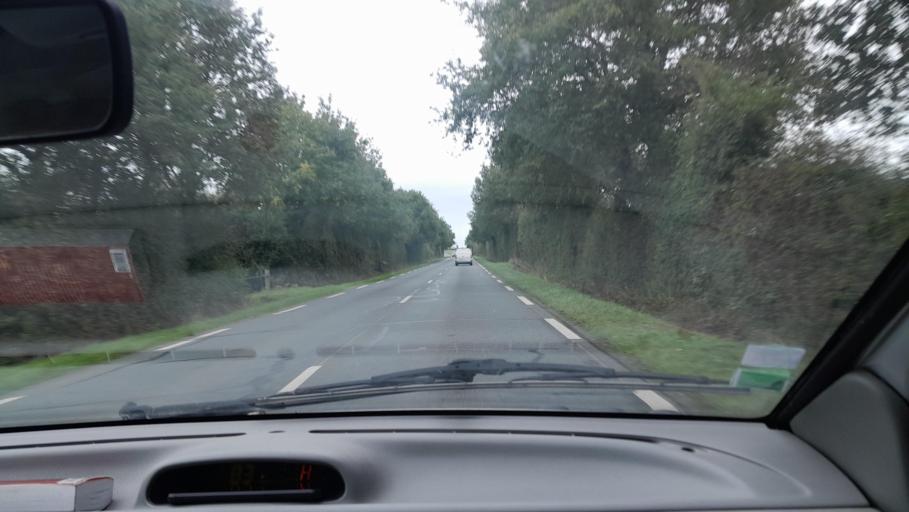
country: FR
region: Pays de la Loire
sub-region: Departement de la Loire-Atlantique
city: Saint-Mars-la-Jaille
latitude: 47.5634
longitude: -1.1870
